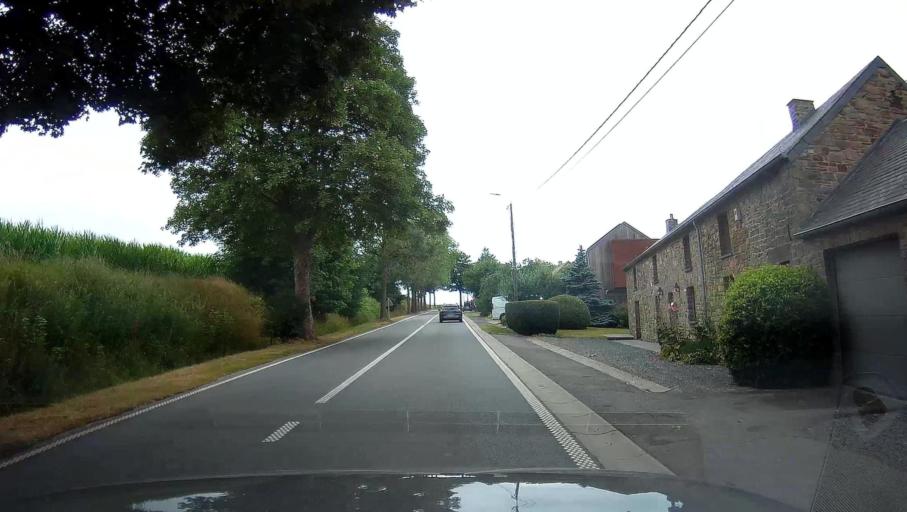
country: BE
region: Wallonia
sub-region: Province de Namur
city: Assesse
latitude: 50.3502
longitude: 5.0437
